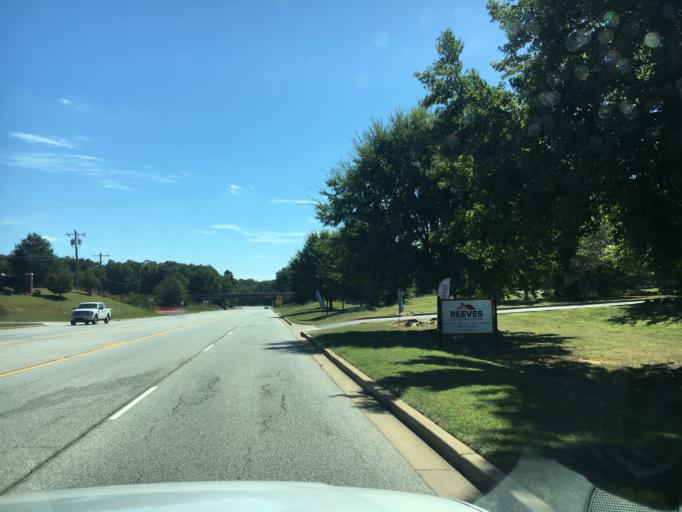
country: US
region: South Carolina
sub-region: Spartanburg County
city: Roebuck
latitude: 34.9079
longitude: -81.9494
